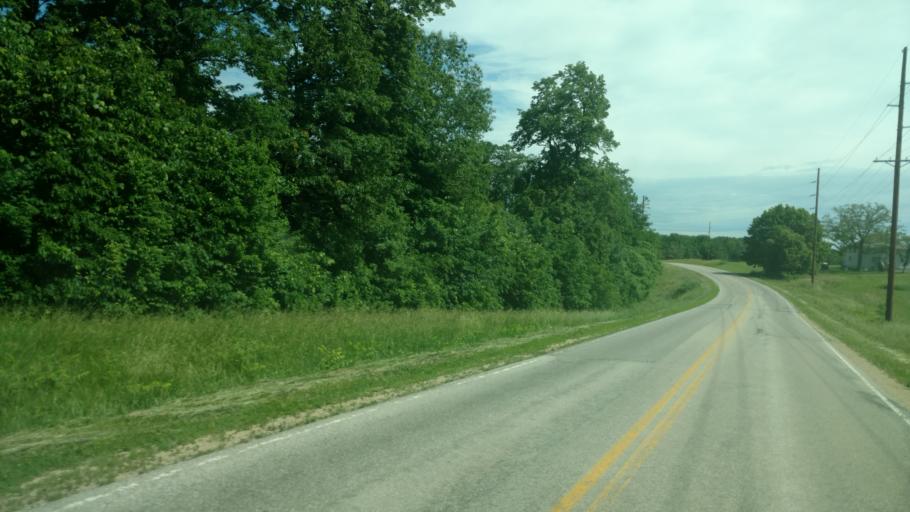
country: US
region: Wisconsin
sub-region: Vernon County
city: Hillsboro
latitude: 43.6758
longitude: -90.4551
